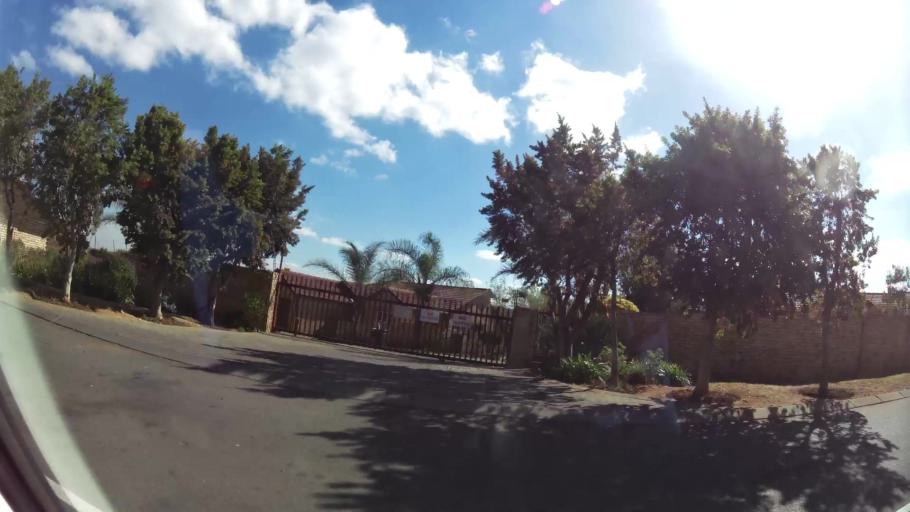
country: ZA
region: Gauteng
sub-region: City of Johannesburg Metropolitan Municipality
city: Midrand
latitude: -25.9936
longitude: 28.0996
